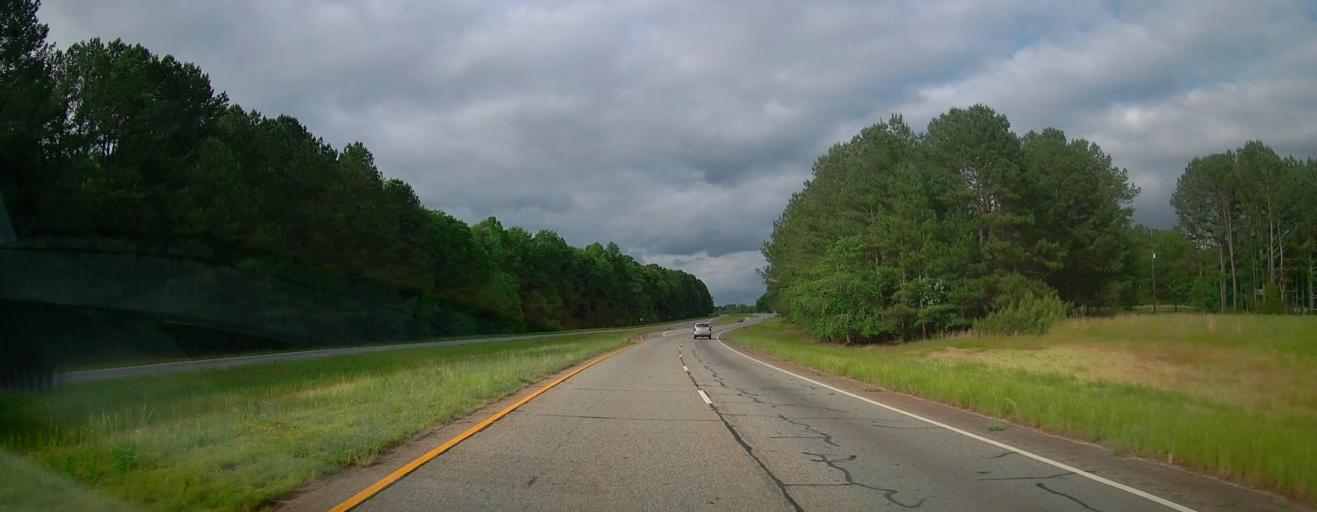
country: US
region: Georgia
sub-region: Barrow County
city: Statham
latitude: 33.8873
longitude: -83.5874
